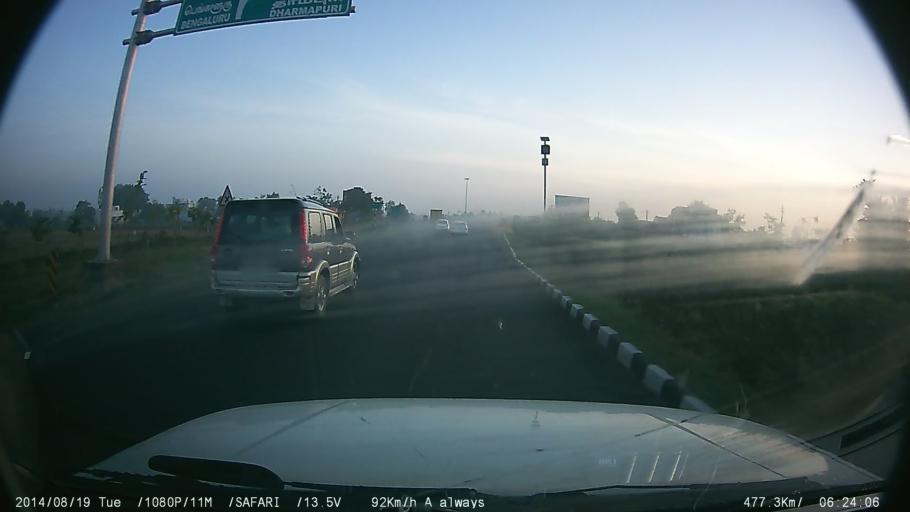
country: IN
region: Tamil Nadu
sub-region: Dharmapuri
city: Dharmapuri
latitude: 12.0471
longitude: 78.1061
